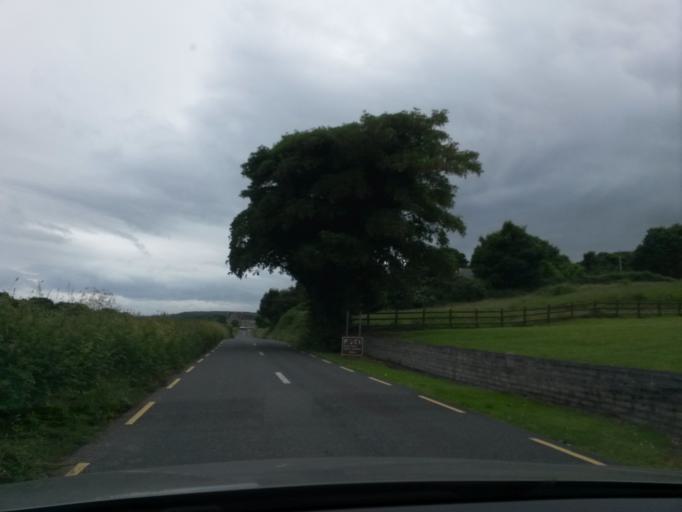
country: IE
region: Connaught
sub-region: Sligo
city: Sligo
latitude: 54.2648
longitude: -8.3294
